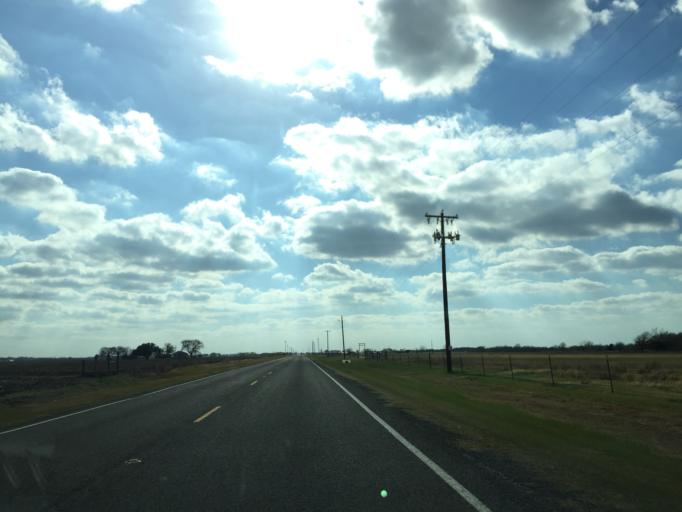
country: US
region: Texas
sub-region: Williamson County
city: Granger
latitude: 30.6712
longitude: -97.3544
